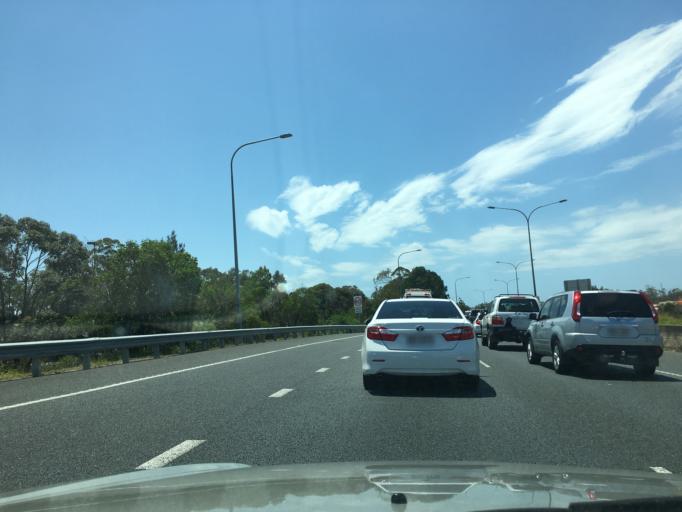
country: AU
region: Queensland
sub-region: Brisbane
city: Wavell Heights
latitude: -27.3781
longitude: 153.0945
